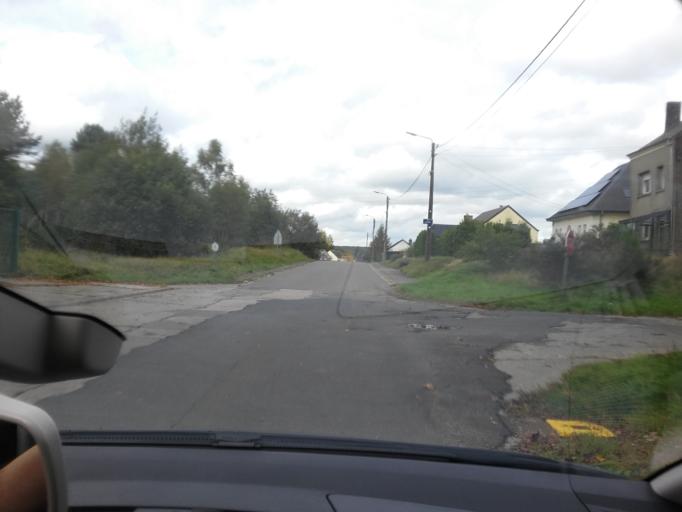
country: BE
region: Wallonia
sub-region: Province du Luxembourg
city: Arlon
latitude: 49.6796
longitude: 5.7718
